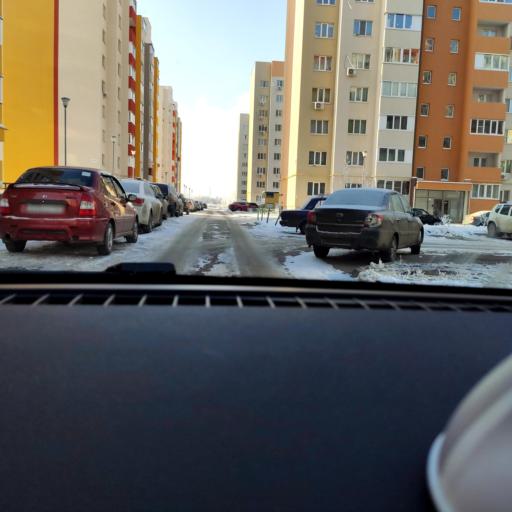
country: RU
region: Samara
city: Samara
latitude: 53.0929
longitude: 50.1621
